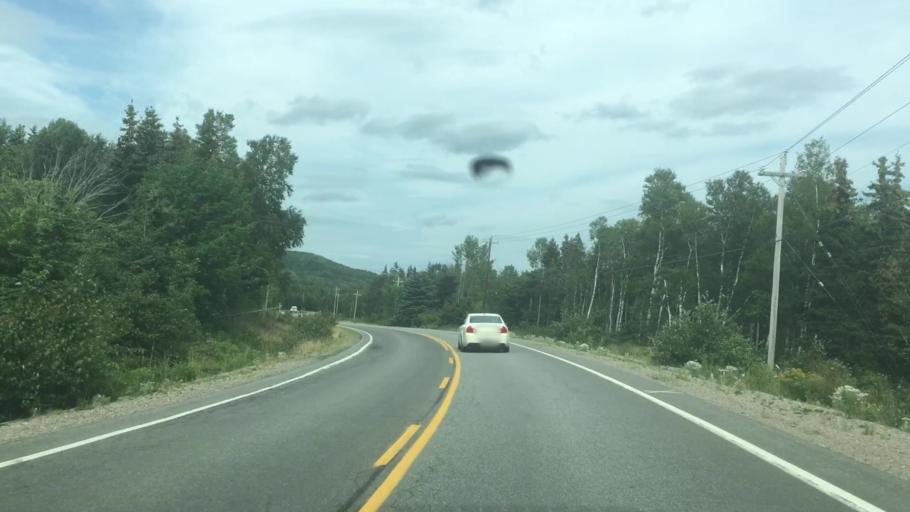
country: CA
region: Nova Scotia
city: Sydney Mines
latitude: 46.5084
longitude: -60.4316
